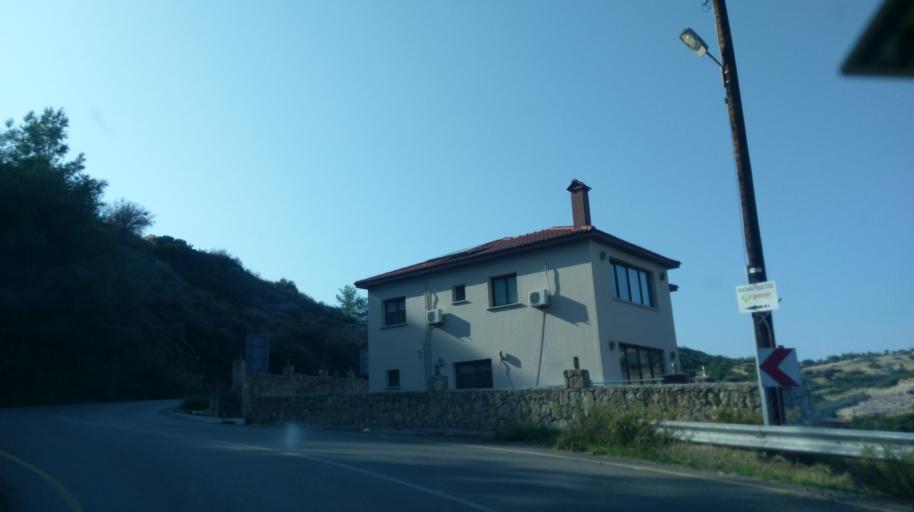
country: CY
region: Lefkosia
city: Kato Pyrgos
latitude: 35.1678
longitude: 32.7306
